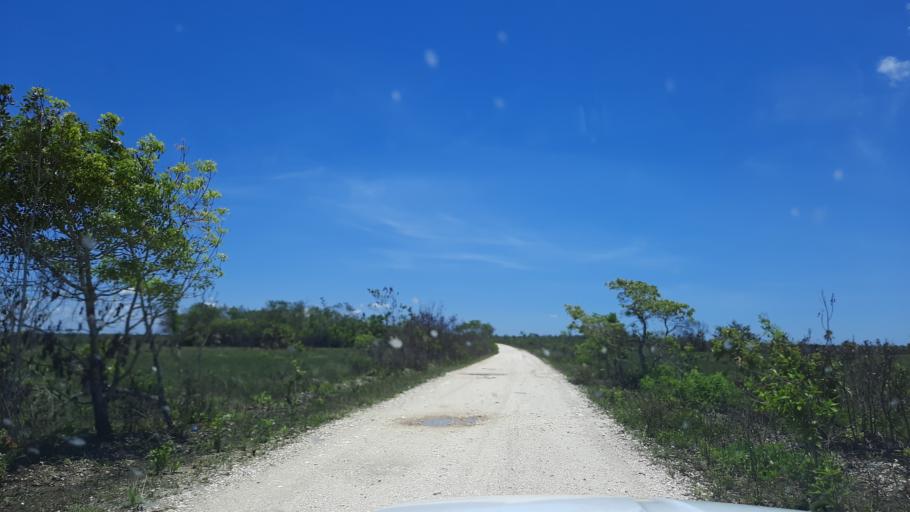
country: BZ
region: Cayo
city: Belmopan
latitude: 17.3895
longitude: -88.4913
